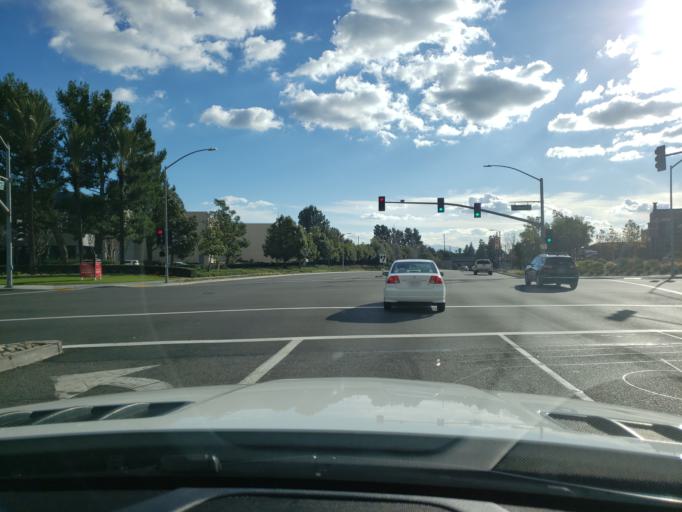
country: US
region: California
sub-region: San Bernardino County
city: Rancho Cucamonga
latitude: 34.0949
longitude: -117.5559
